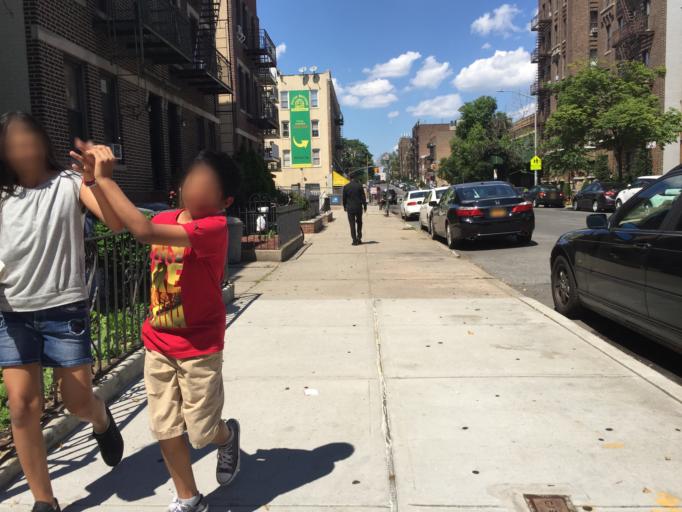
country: US
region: New York
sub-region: Queens County
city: Long Island City
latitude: 40.7654
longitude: -73.9206
